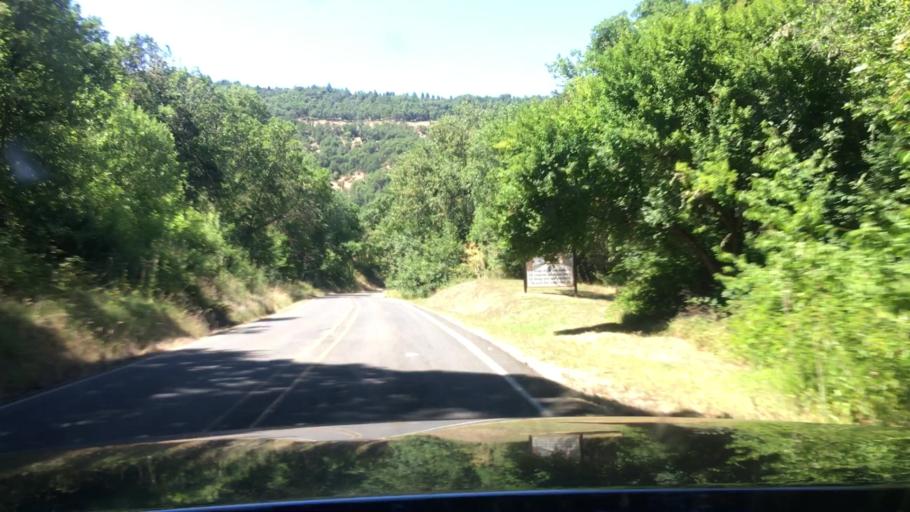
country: US
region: Oregon
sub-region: Douglas County
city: Winston
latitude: 43.1407
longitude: -123.4142
